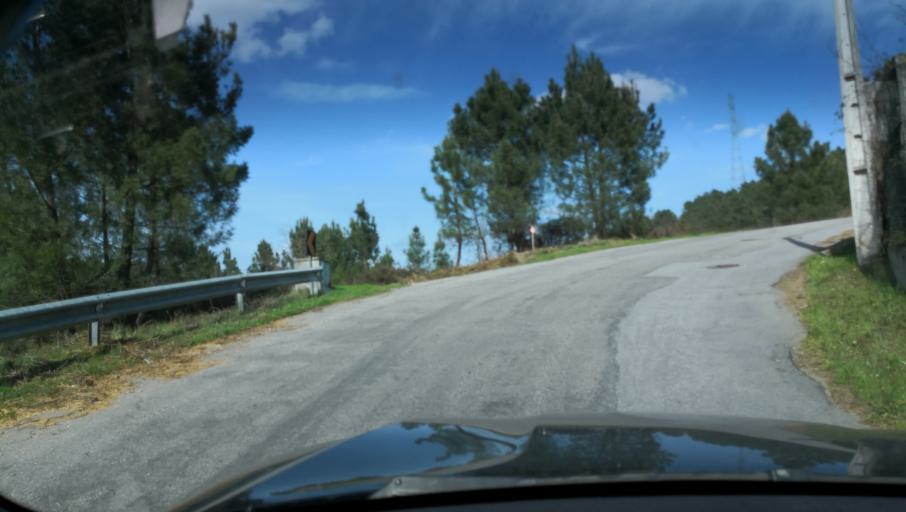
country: PT
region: Vila Real
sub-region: Vila Real
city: Vila Real
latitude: 41.2542
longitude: -7.6816
